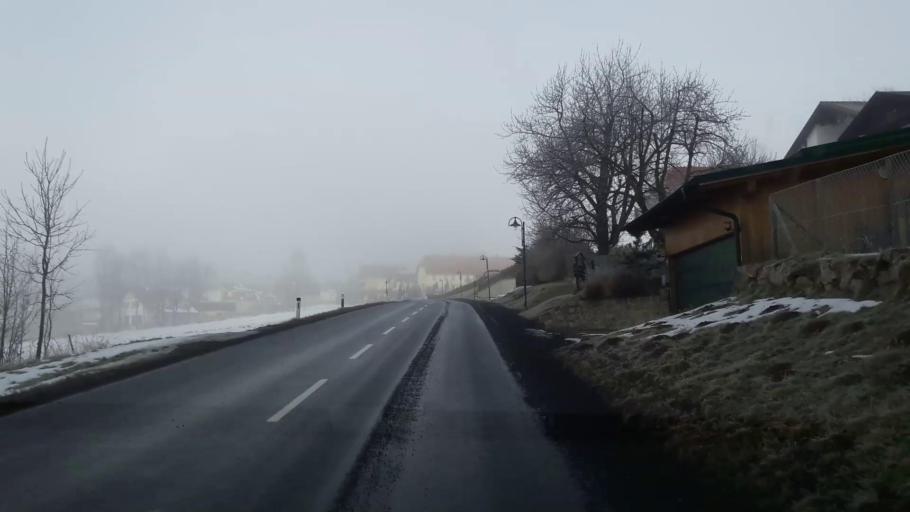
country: AT
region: Lower Austria
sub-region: Politischer Bezirk Neunkirchen
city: Sankt Corona am Wechsel
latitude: 47.5752
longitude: 16.0281
